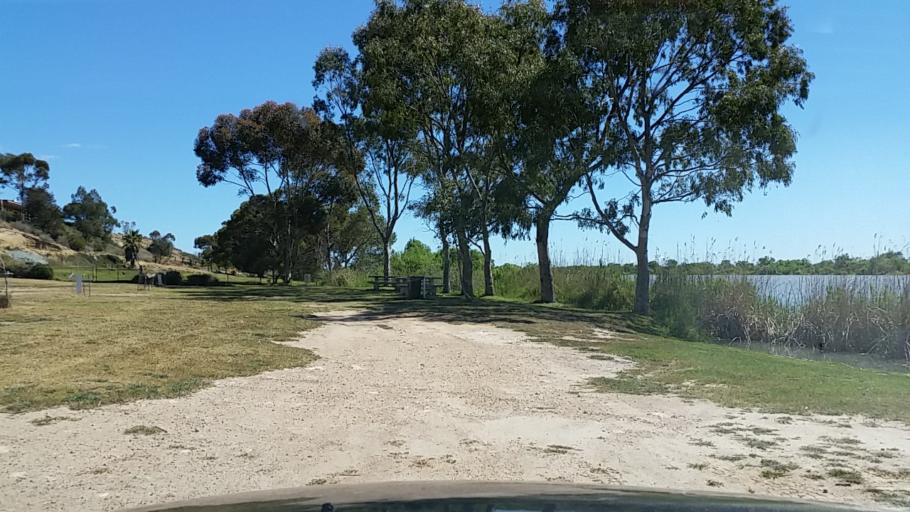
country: AU
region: South Australia
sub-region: Murray Bridge
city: Tailem Bend
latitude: -35.2869
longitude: 139.4476
